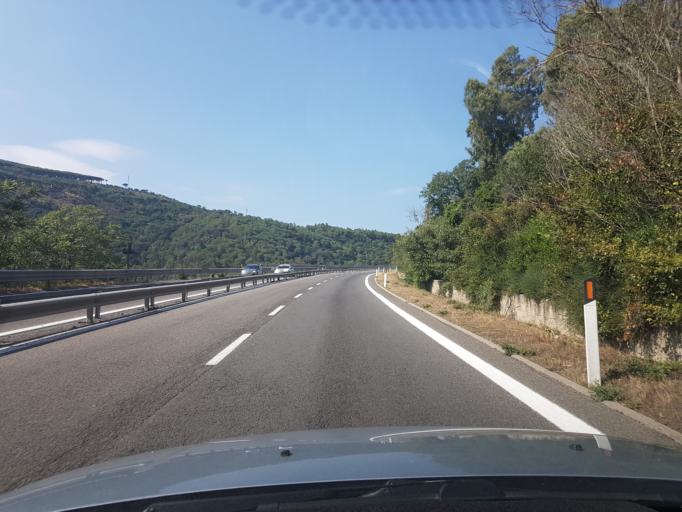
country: IT
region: Sardinia
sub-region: Provincia di Nuoro
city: Nuoro
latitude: 40.3361
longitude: 9.2995
